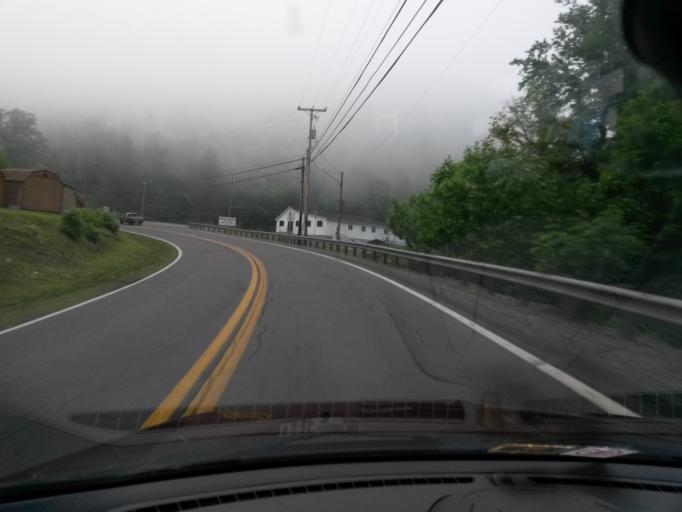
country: US
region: West Virginia
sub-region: McDowell County
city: Welch
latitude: 37.5023
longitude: -81.5531
